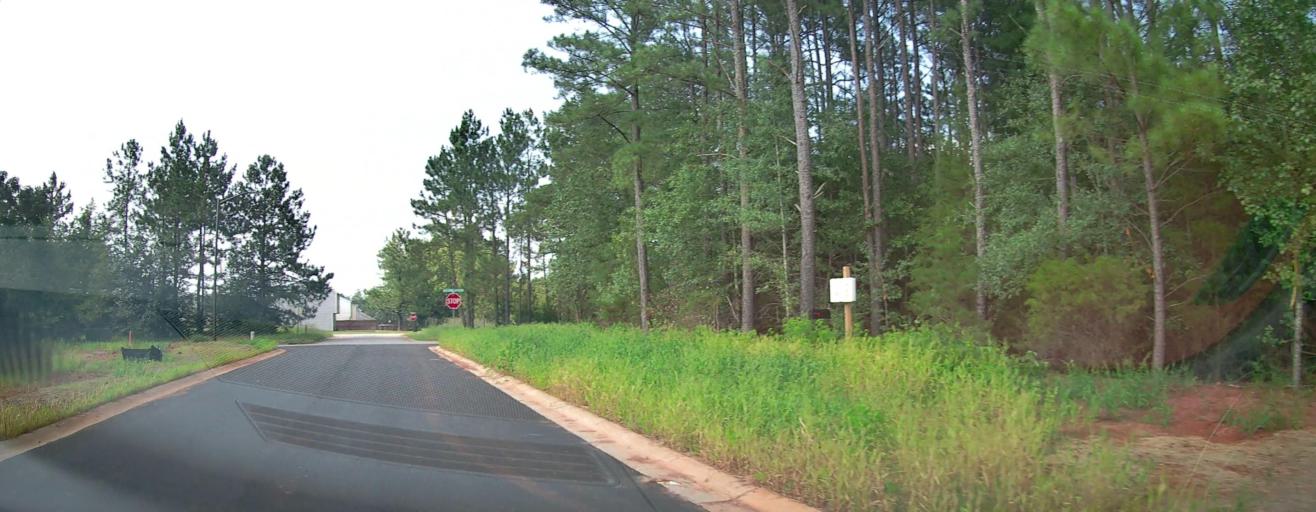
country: US
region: Georgia
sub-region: Houston County
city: Centerville
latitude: 32.6498
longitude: -83.7032
